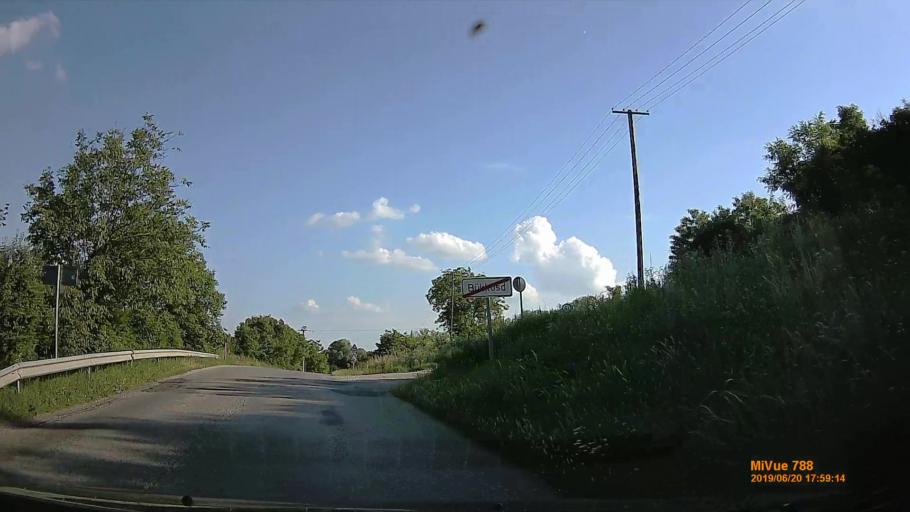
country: HU
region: Baranya
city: Buekkoesd
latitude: 46.0989
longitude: 17.9867
